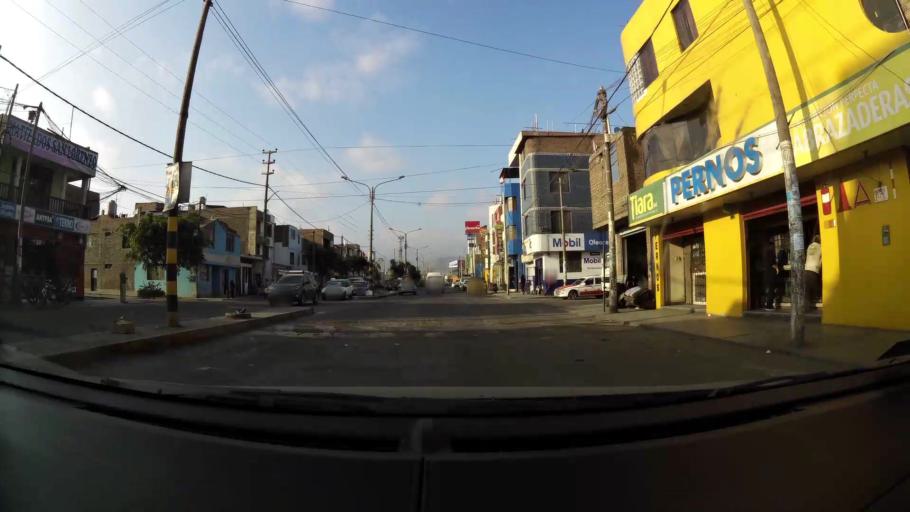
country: PE
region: La Libertad
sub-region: Provincia de Trujillo
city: El Porvenir
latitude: -8.0920
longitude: -79.0077
